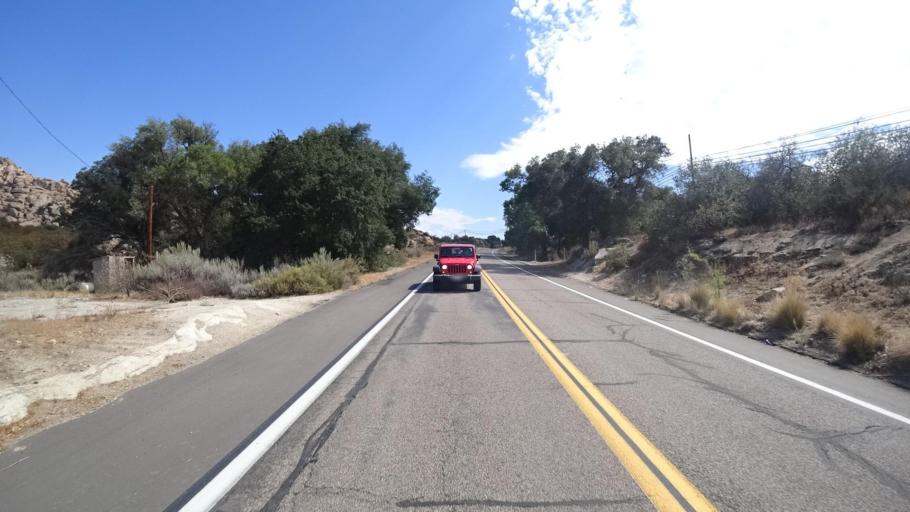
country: MX
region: Baja California
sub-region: Tecate
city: Cereso del Hongo
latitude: 32.6531
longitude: -116.2452
